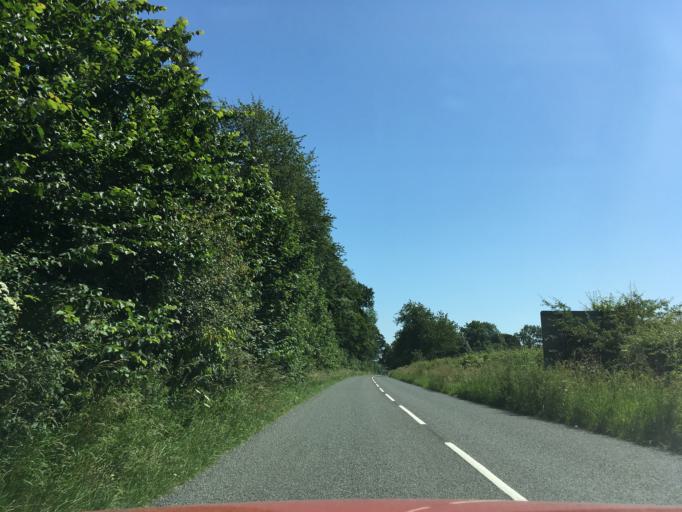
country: GB
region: England
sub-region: Oxfordshire
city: Hook Norton
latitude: 51.9824
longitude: -1.4277
